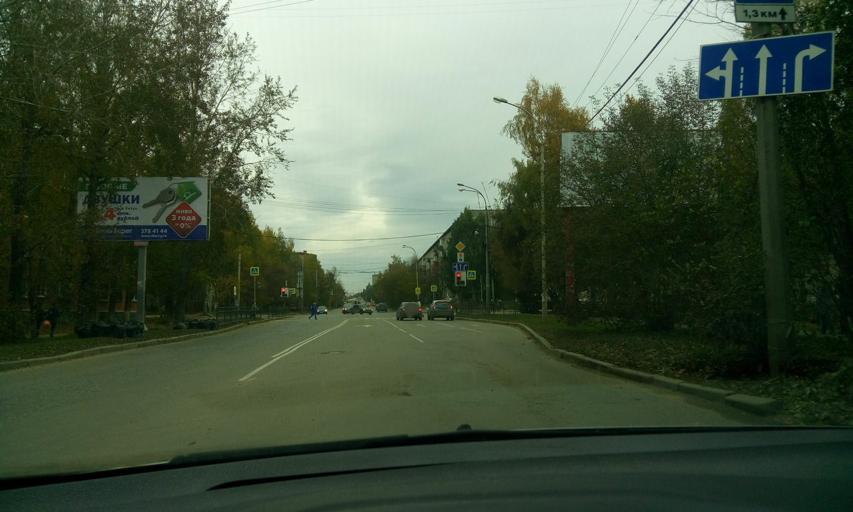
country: RU
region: Sverdlovsk
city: Yekaterinburg
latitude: 56.8616
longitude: 60.6533
